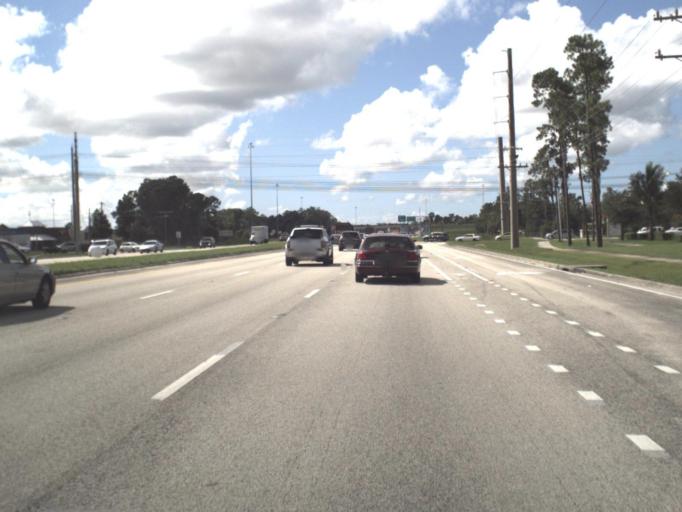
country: US
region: Florida
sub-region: Sarasota County
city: Desoto Lakes
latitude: 27.4390
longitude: -82.4520
